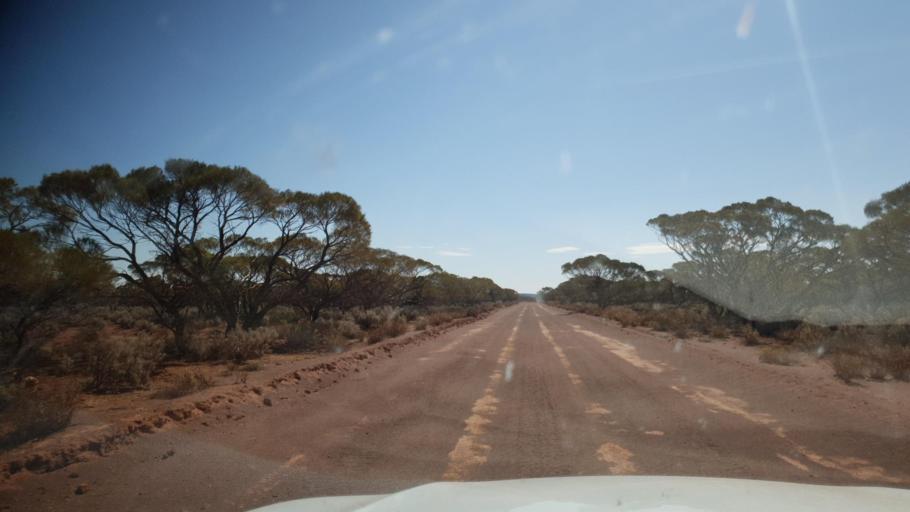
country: AU
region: South Australia
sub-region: Kimba
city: Caralue
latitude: -32.4858
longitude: 136.0553
